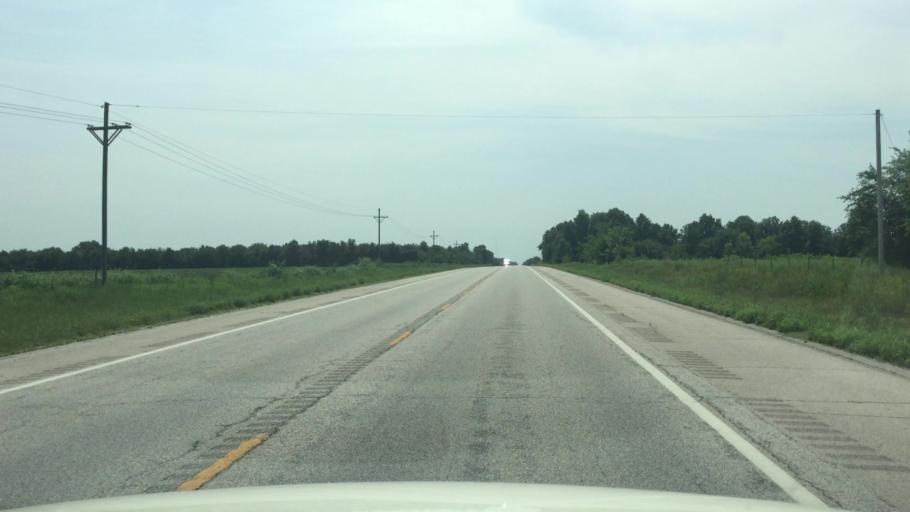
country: US
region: Kansas
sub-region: Cherokee County
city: Galena
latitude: 37.1571
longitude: -94.7043
